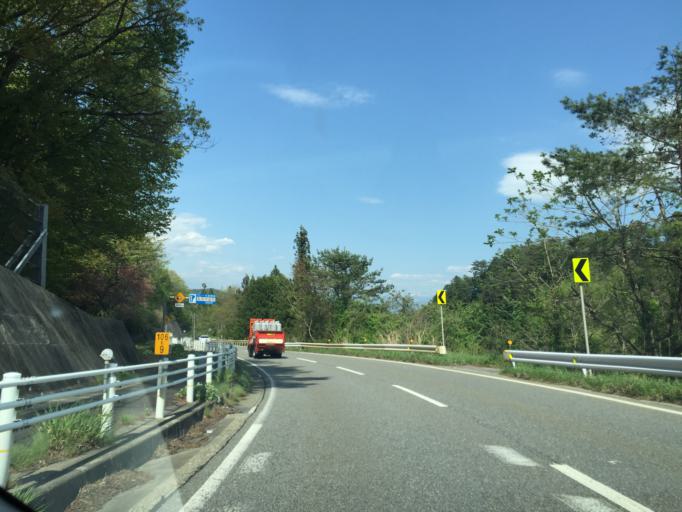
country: JP
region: Nagano
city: Iida
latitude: 35.4377
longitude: 137.7078
